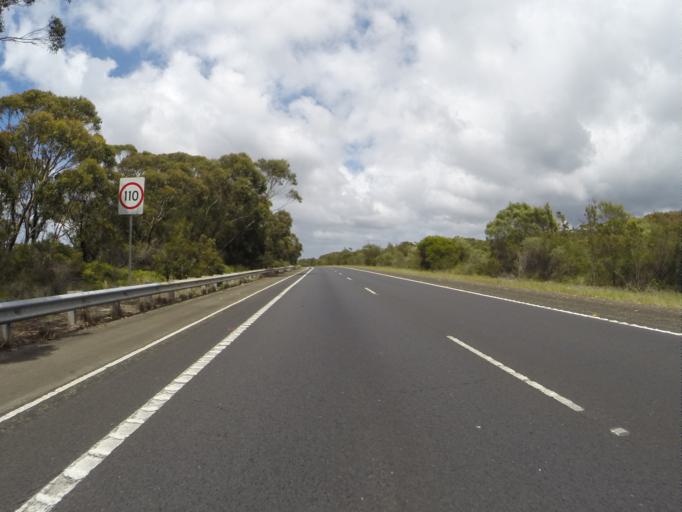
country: AU
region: New South Wales
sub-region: Wollongong
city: Helensburgh
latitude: -34.2453
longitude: 150.9402
